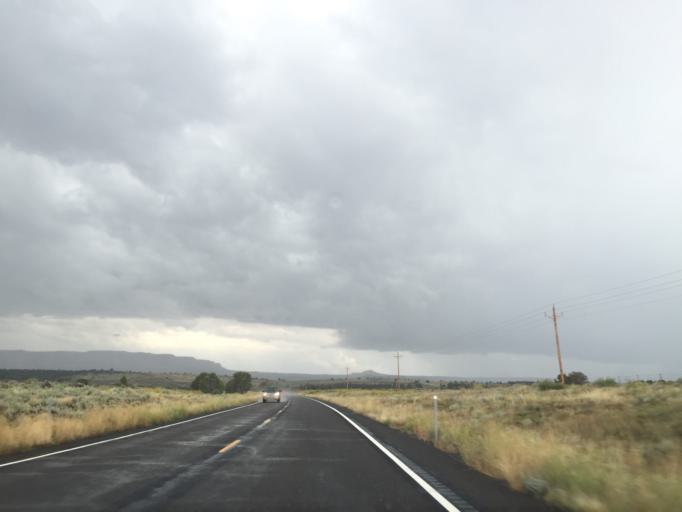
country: US
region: Utah
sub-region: Kane County
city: Kanab
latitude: 37.2386
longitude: -112.7476
